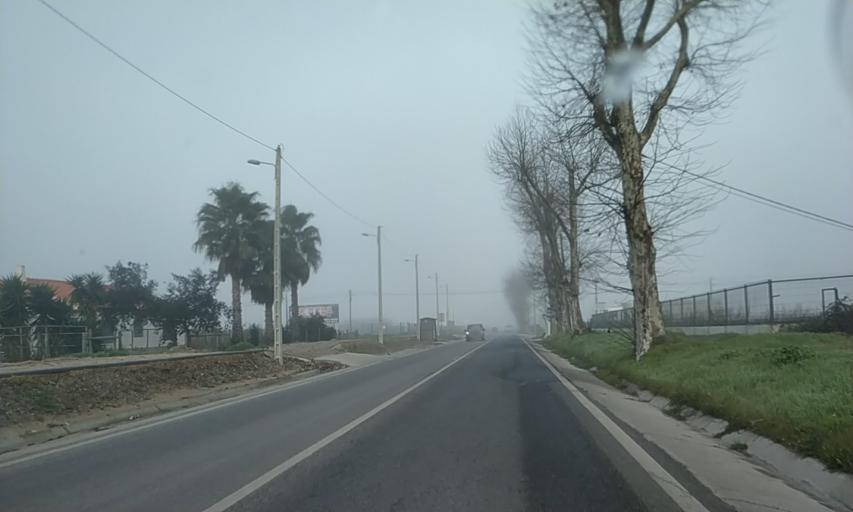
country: PT
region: Setubal
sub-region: Palmela
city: Pinhal Novo
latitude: 38.6565
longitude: -8.9197
